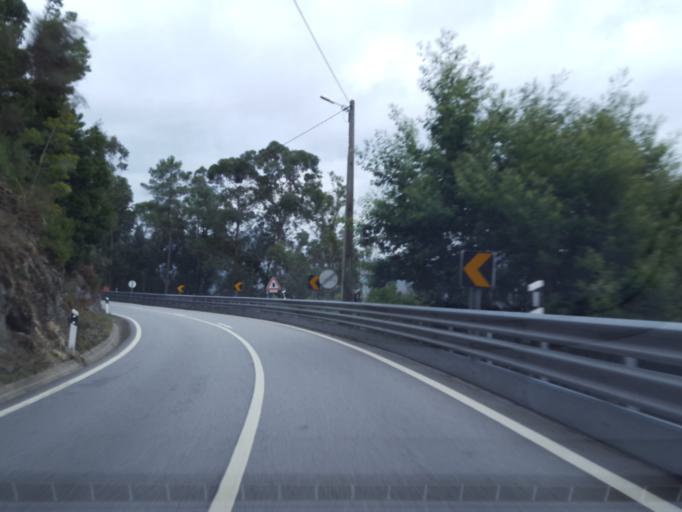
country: PT
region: Porto
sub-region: Marco de Canaveses
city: Marco de Canavezes
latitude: 41.1406
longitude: -8.1269
